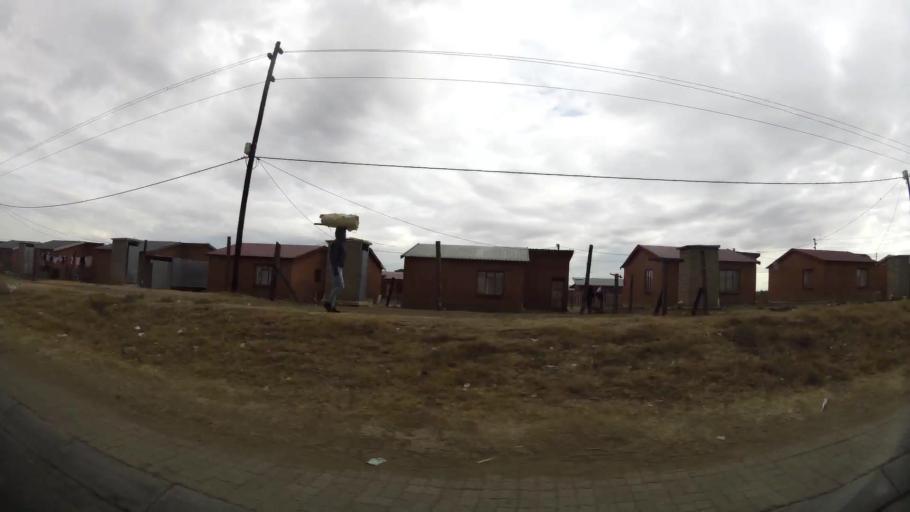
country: ZA
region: Orange Free State
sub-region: Fezile Dabi District Municipality
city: Kroonstad
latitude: -27.6538
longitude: 27.2228
